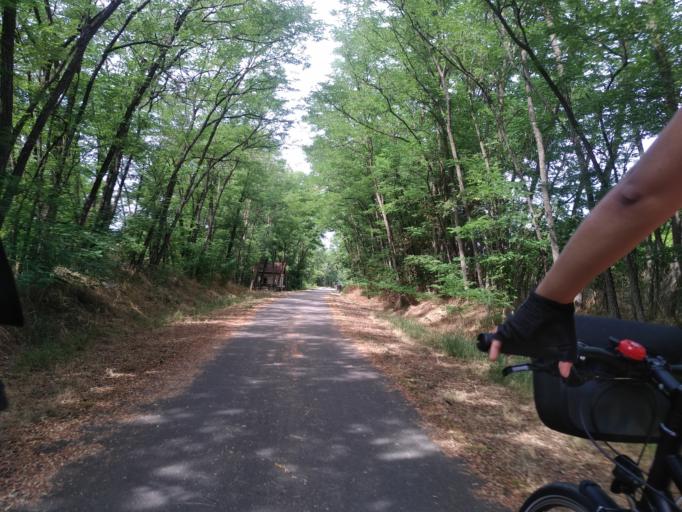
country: FR
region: Auvergne
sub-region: Departement de l'Allier
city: Diou
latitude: 46.5506
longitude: 3.7416
